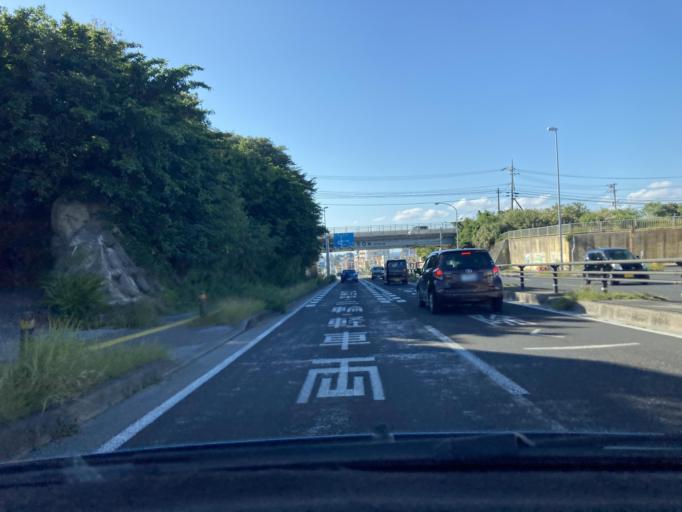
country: JP
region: Okinawa
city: Ginowan
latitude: 26.2546
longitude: 127.7346
